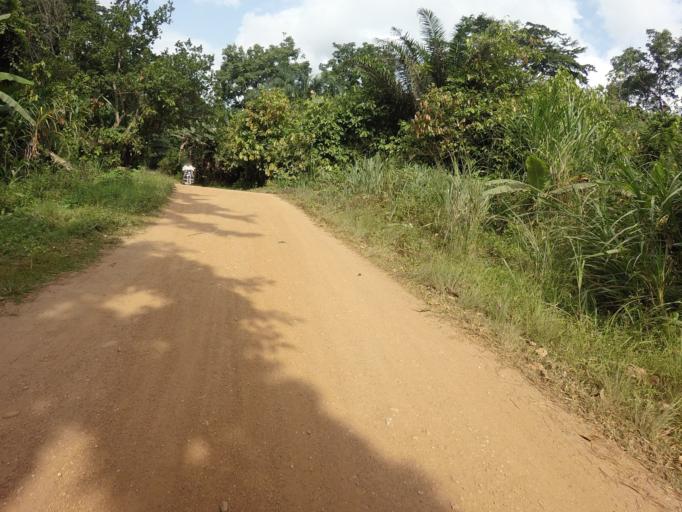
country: GH
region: Volta
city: Kpandu
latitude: 6.8900
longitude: 0.4354
